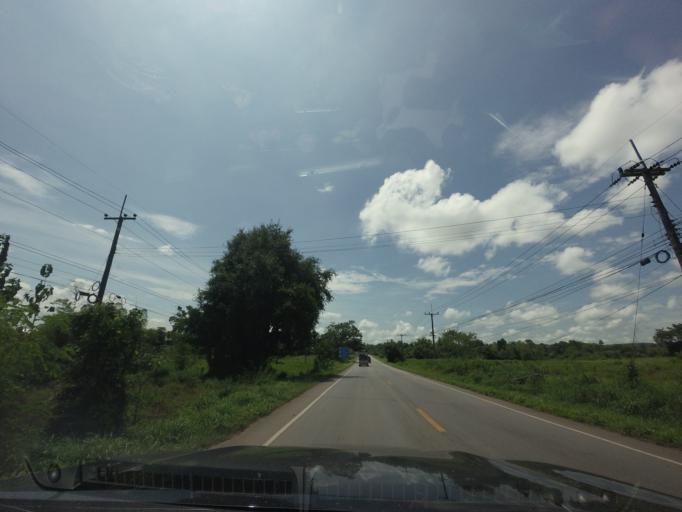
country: TH
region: Changwat Udon Thani
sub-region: Amphoe Ban Phue
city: Ban Phue
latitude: 17.7215
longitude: 102.3931
